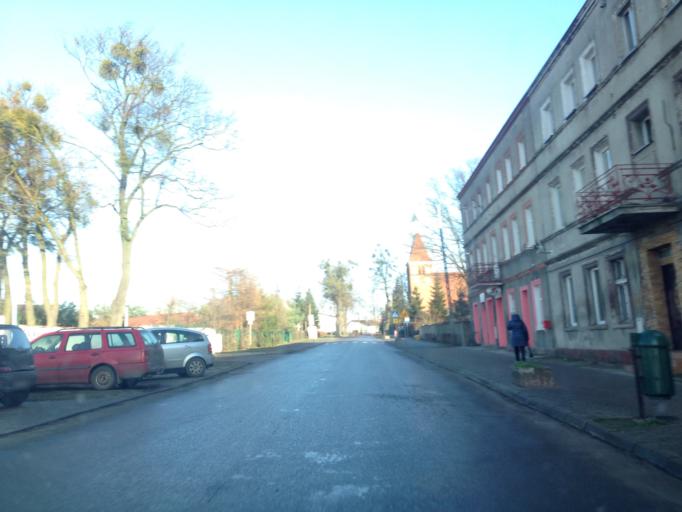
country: PL
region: Kujawsko-Pomorskie
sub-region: Powiat brodnicki
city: Jablonowo Pomorskie
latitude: 53.3930
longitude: 19.1560
